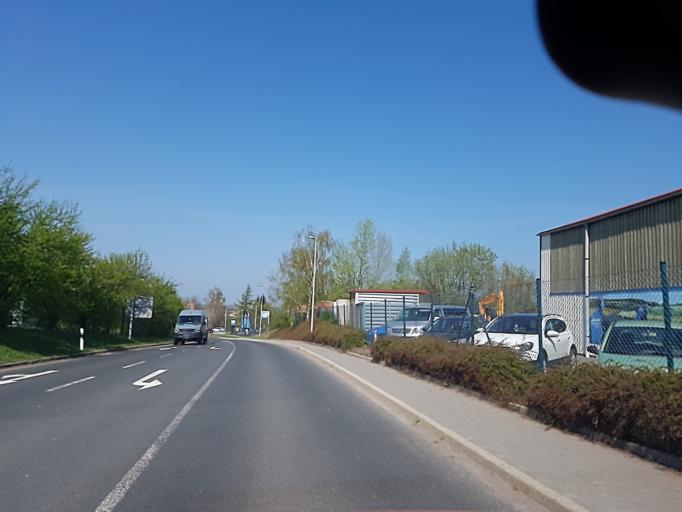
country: DE
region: Saxony
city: Leisnig
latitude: 51.1587
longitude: 12.9148
